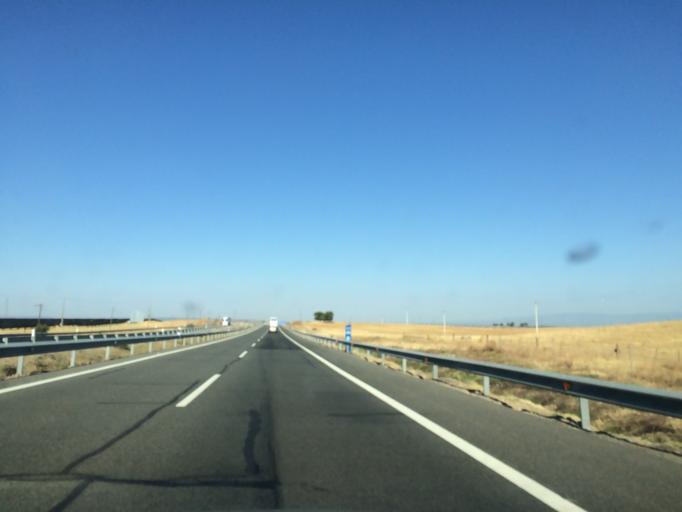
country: ES
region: Castille-La Mancha
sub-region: Province of Toledo
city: Caleruela
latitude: 39.8953
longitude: -5.3089
